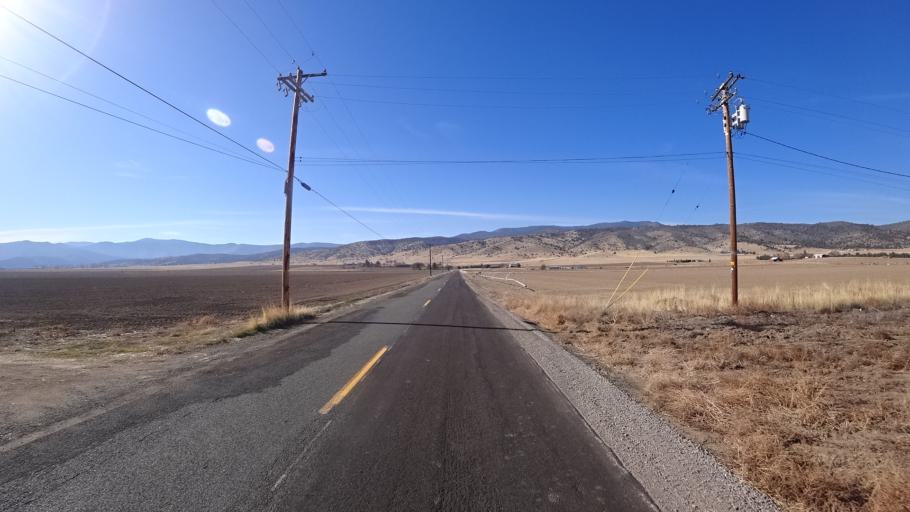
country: US
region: California
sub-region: Siskiyou County
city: Montague
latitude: 41.5747
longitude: -122.5396
